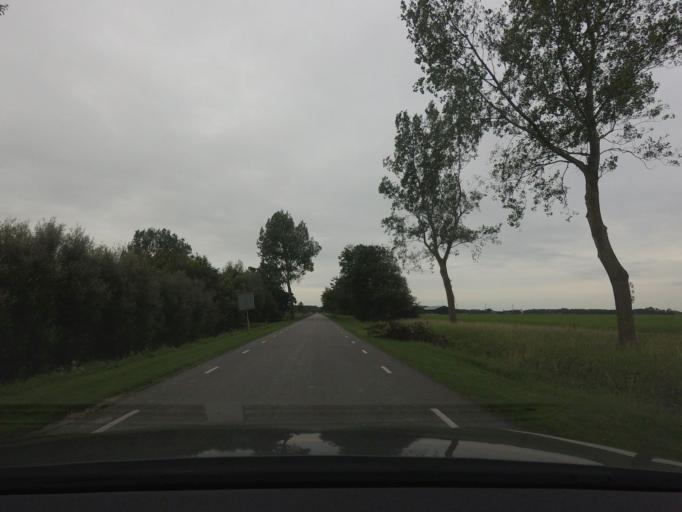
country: NL
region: North Holland
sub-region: Gemeente Schagen
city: Harenkarspel
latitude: 52.7082
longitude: 4.7389
